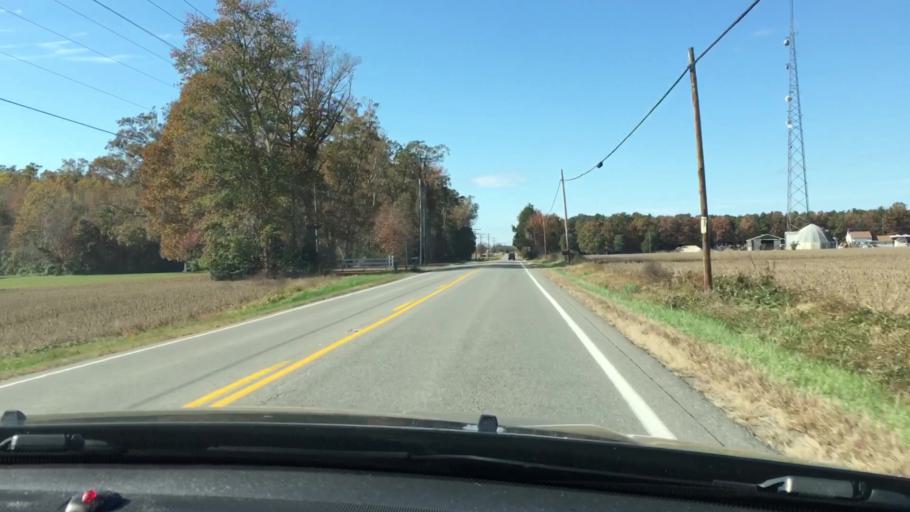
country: US
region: Virginia
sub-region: King William County
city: Central Garage
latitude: 37.7197
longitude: -77.0785
